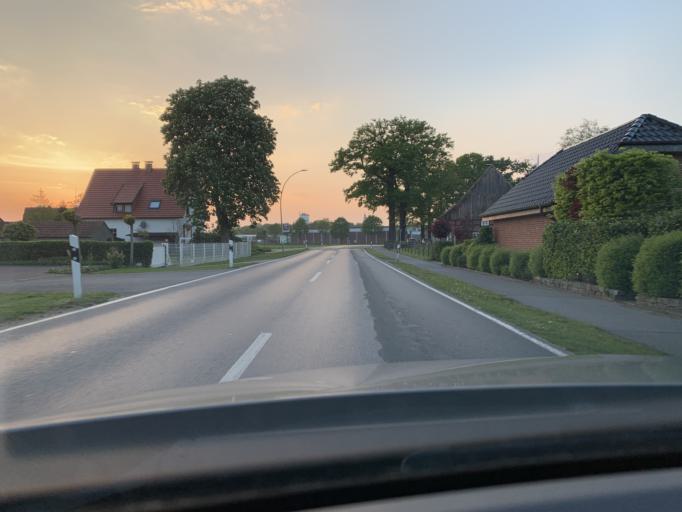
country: DE
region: North Rhine-Westphalia
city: Rietberg
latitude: 51.7588
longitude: 8.3882
